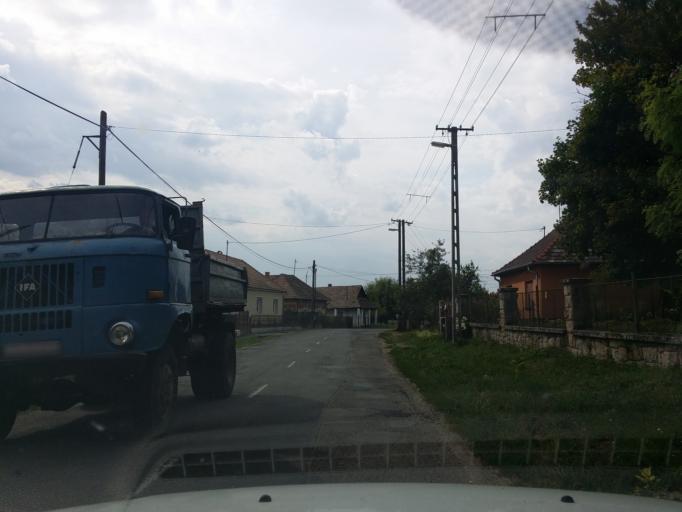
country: HU
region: Nograd
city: Bercel
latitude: 47.9827
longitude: 19.3718
